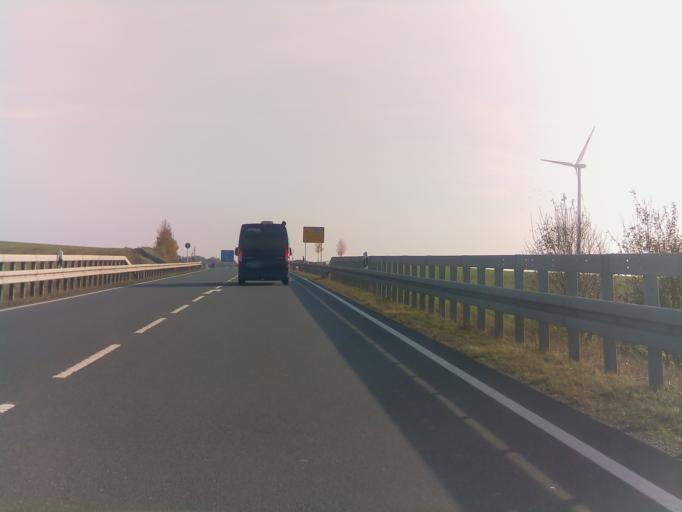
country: DE
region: Bavaria
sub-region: Regierungsbezirk Unterfranken
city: Biebelried
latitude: 49.7642
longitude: 10.0941
